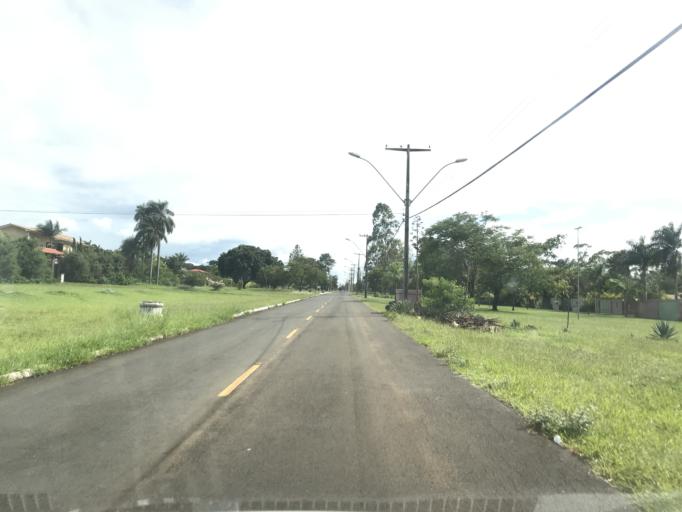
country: BR
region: Federal District
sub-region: Brasilia
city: Brasilia
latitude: -15.8914
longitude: -47.9185
